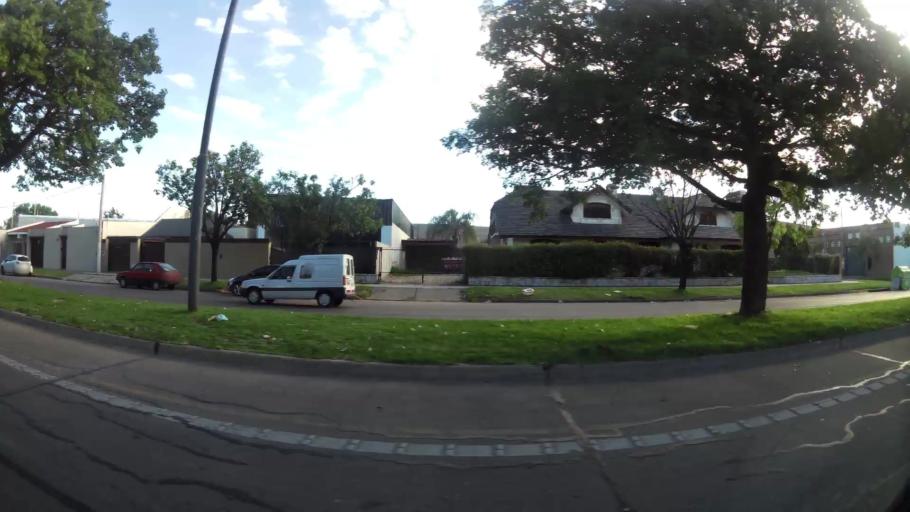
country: AR
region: Santa Fe
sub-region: Departamento de Rosario
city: Rosario
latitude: -32.9752
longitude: -60.6680
